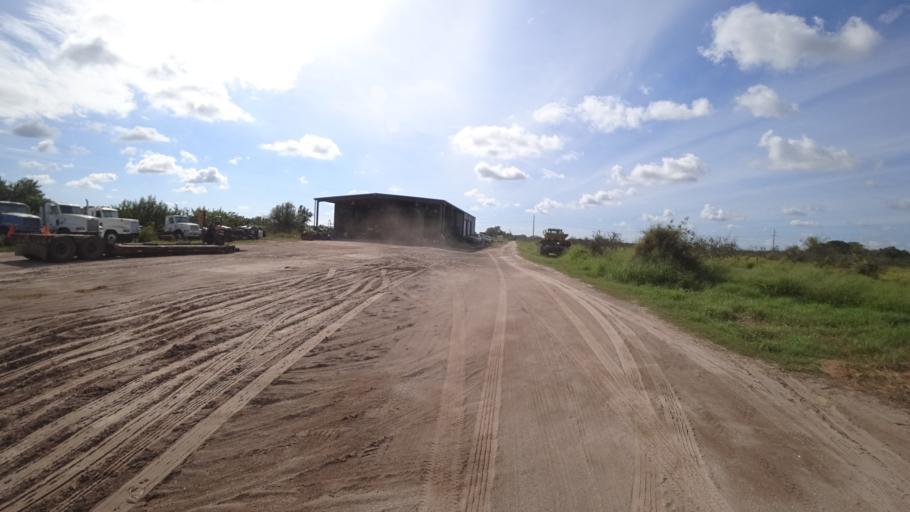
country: US
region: Florida
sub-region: Hillsborough County
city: Wimauma
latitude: 27.6059
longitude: -82.2880
